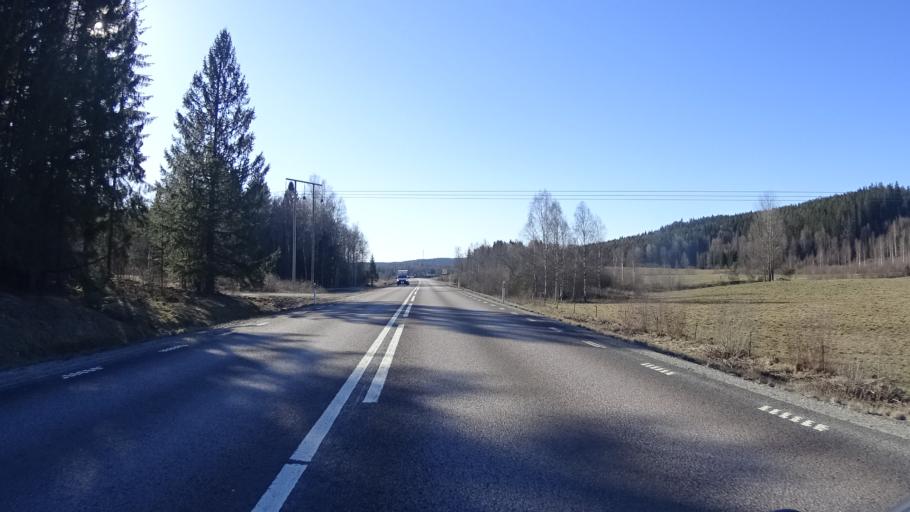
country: SE
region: Vaermland
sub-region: Arvika Kommun
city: Arvika
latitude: 59.6686
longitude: 12.8212
